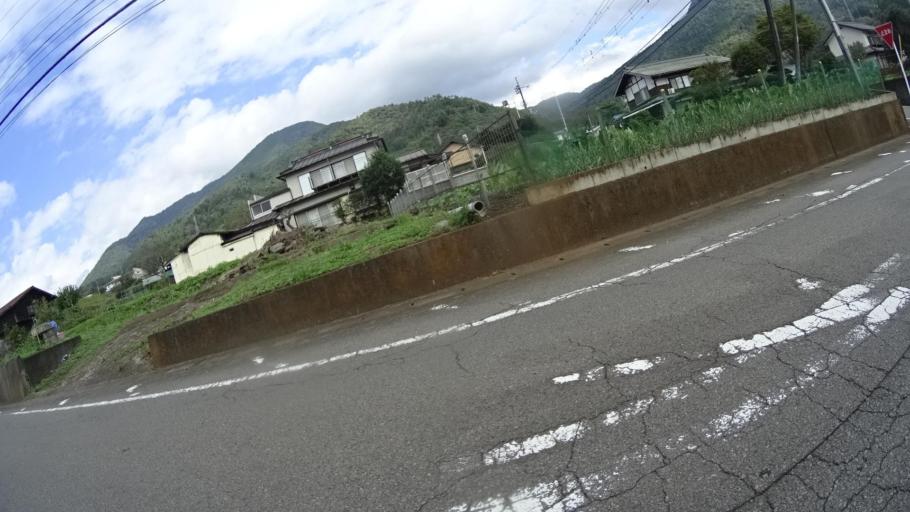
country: JP
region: Yamanashi
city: Otsuki
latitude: 35.6211
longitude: 138.9895
